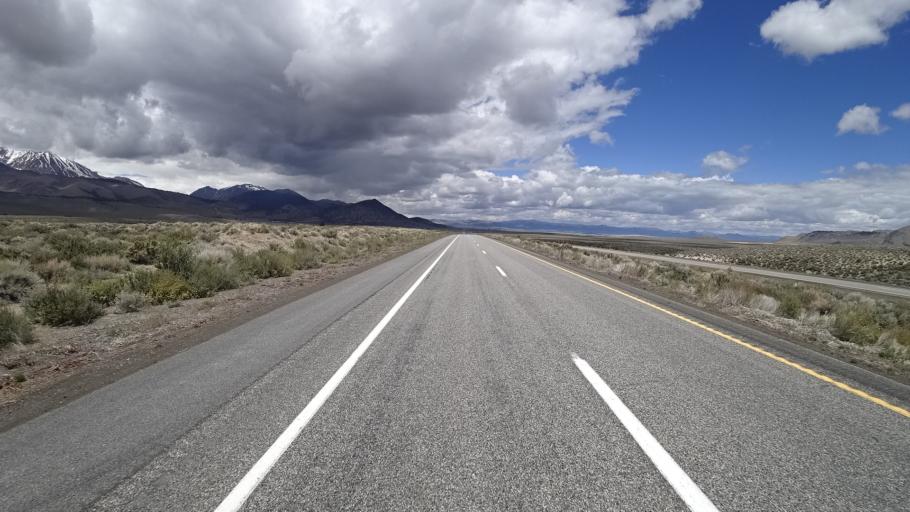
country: US
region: California
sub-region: Mono County
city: Mammoth Lakes
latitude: 37.8665
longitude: -119.0874
